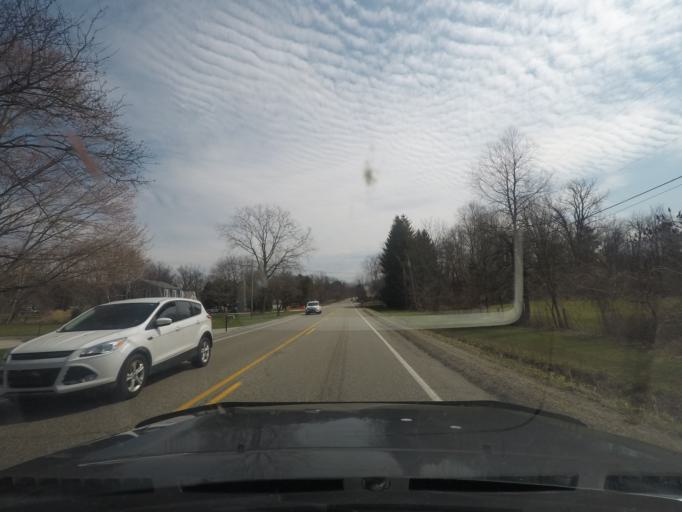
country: US
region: Indiana
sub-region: LaPorte County
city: Trail Creek
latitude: 41.6834
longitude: -86.7930
